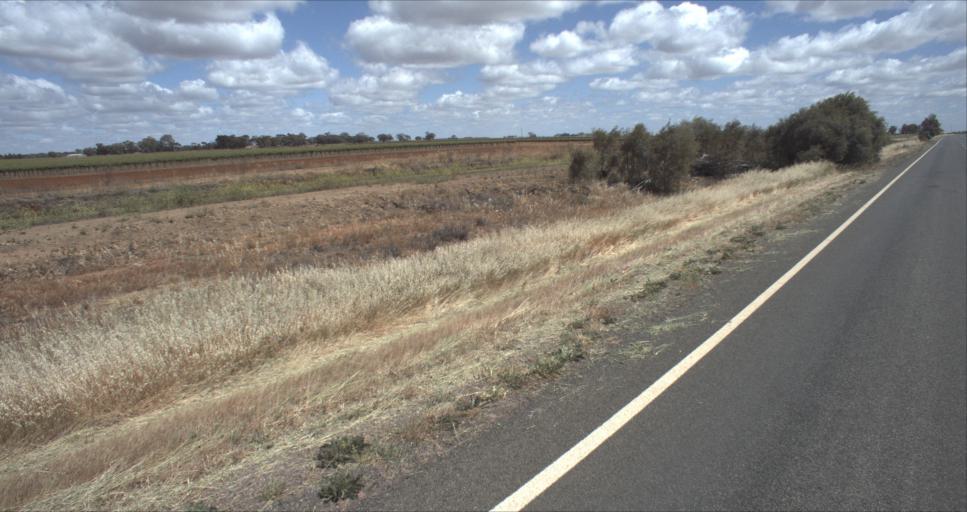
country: AU
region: New South Wales
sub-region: Murrumbidgee Shire
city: Darlington Point
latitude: -34.4808
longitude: 146.1542
